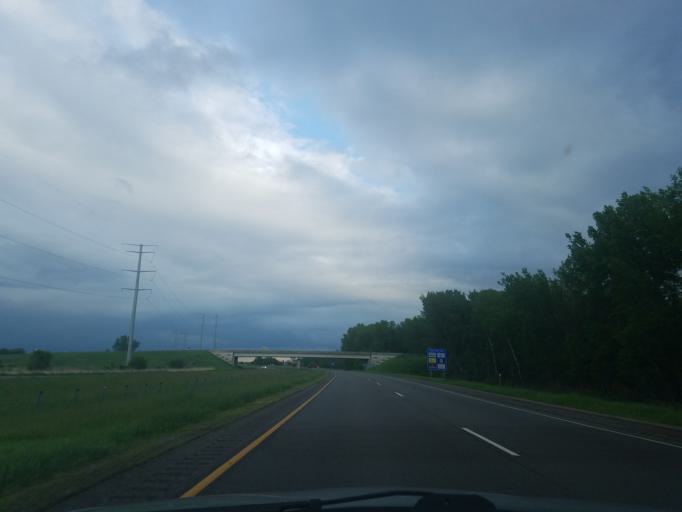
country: US
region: Minnesota
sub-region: Stearns County
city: Waite Park
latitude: 45.5033
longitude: -94.2695
